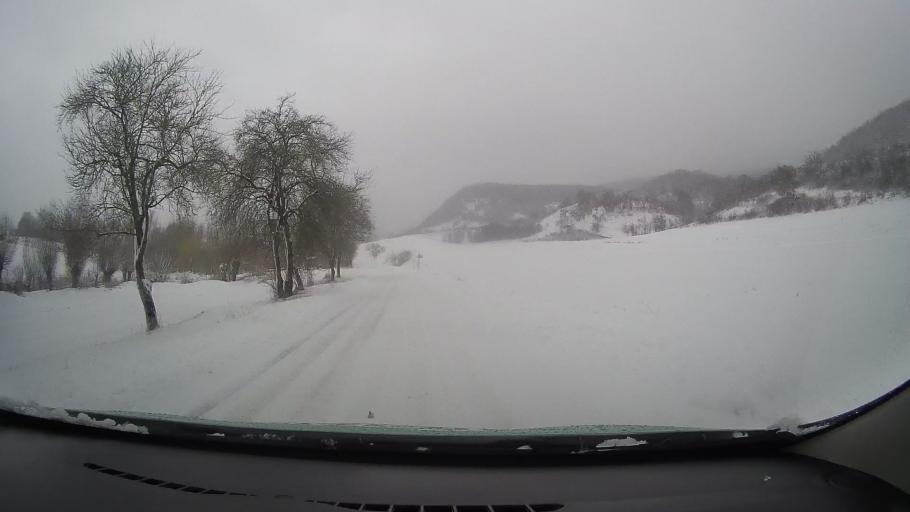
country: RO
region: Hunedoara
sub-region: Comuna Carjiti
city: Carjiti
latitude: 45.8424
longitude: 22.8343
